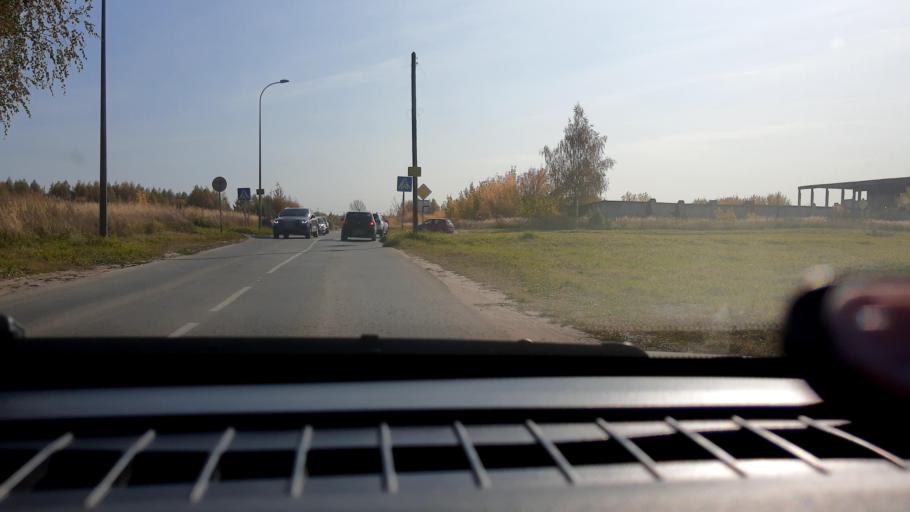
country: RU
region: Nizjnij Novgorod
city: Kstovo
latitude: 56.1511
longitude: 44.2219
